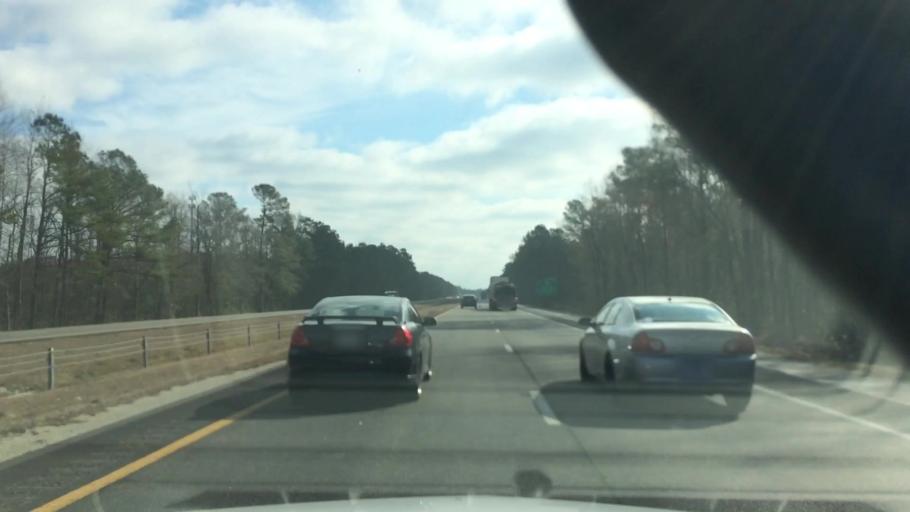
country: US
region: North Carolina
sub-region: Pender County
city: Burgaw
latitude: 34.6051
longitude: -77.9155
